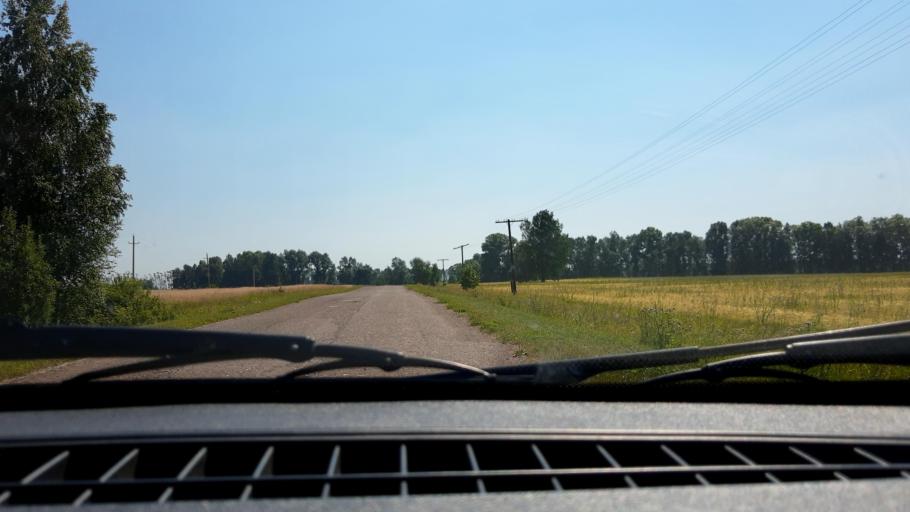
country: RU
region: Bashkortostan
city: Kushnarenkovo
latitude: 55.0652
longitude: 55.1638
